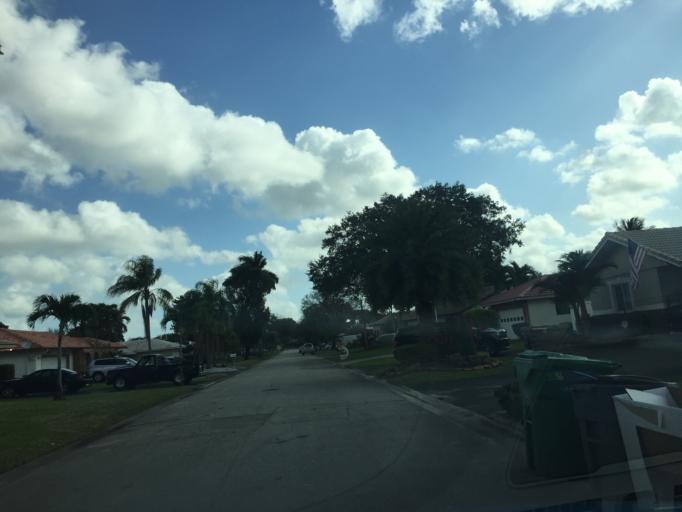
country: US
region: Florida
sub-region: Broward County
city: Tamarac
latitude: 26.2308
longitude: -80.2436
